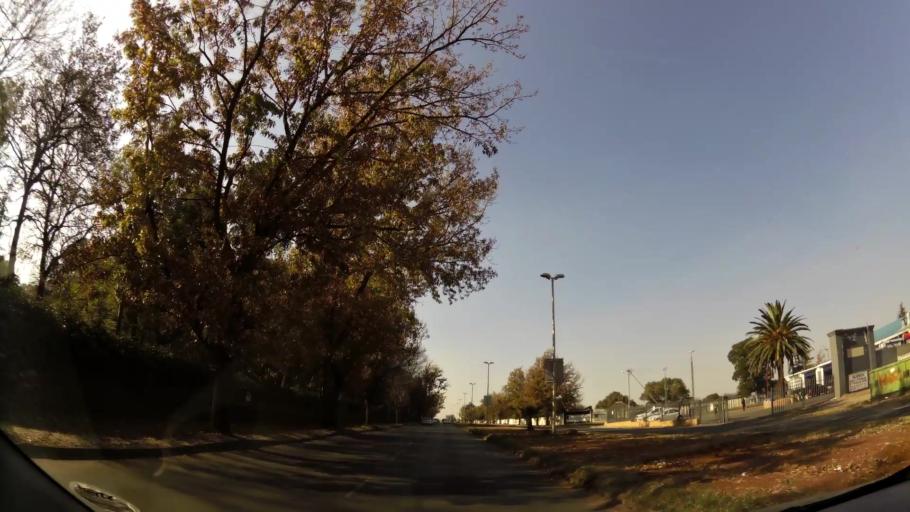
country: ZA
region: Gauteng
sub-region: West Rand District Municipality
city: Randfontein
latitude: -26.1732
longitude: 27.6962
